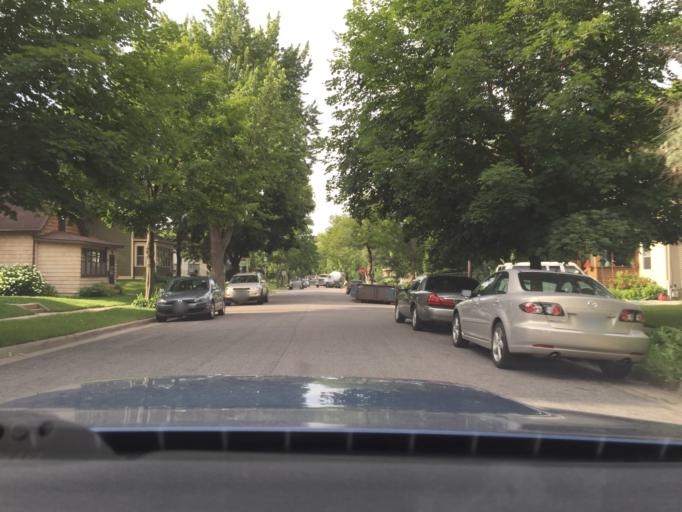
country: US
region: Minnesota
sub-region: Dakota County
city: West Saint Paul
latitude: 44.9215
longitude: -93.1059
